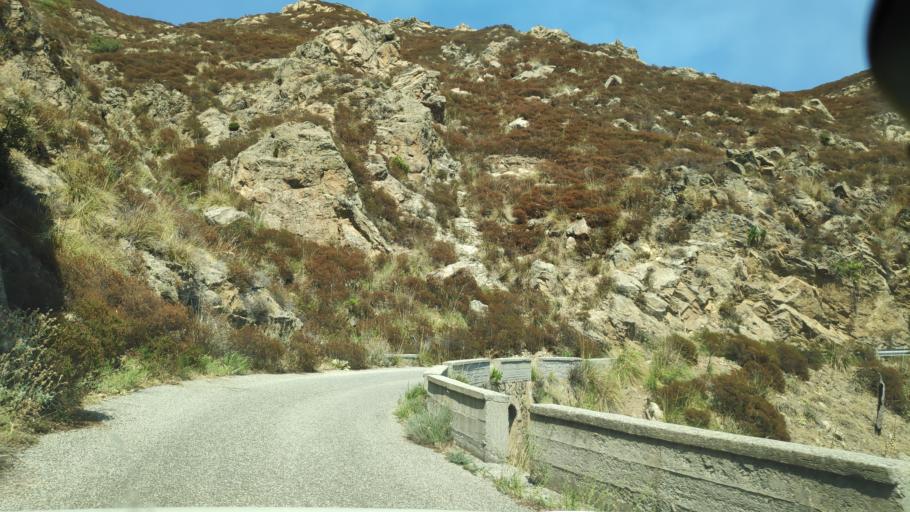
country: IT
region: Calabria
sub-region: Provincia di Reggio Calabria
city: Bova
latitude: 38.0021
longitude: 15.9267
